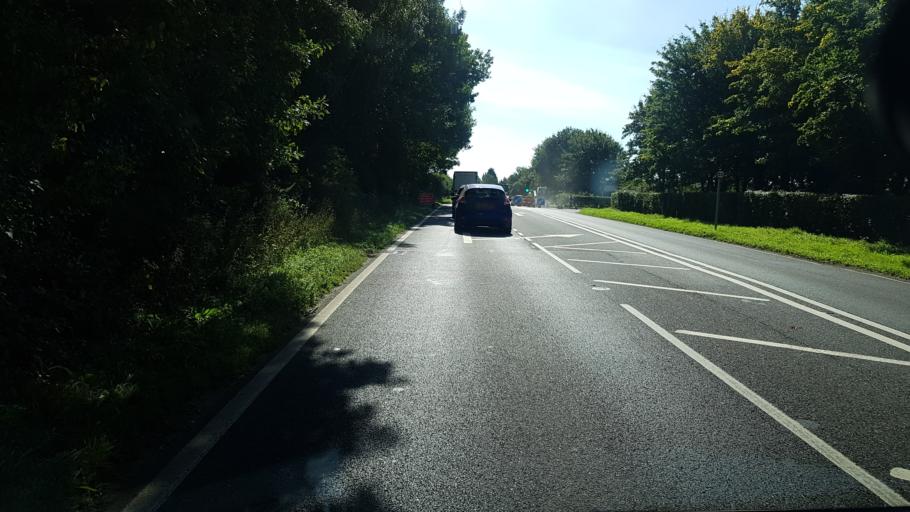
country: GB
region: England
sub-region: Kent
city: Kings Hill
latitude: 51.2693
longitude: 0.3591
